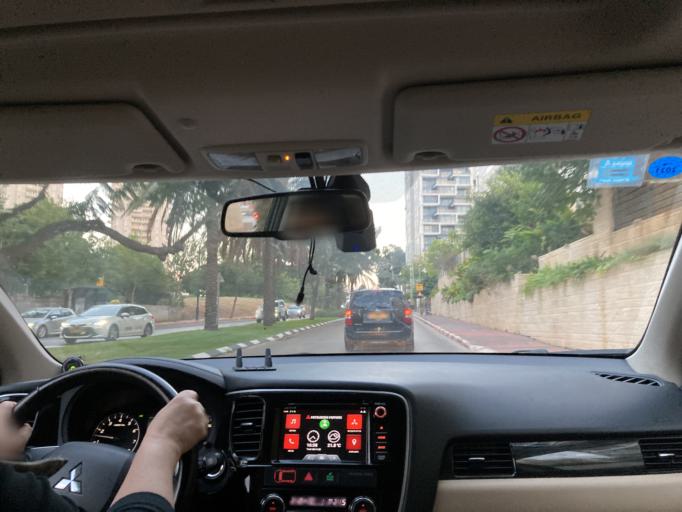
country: IL
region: Tel Aviv
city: Herzliyya
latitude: 32.1599
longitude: 34.8341
